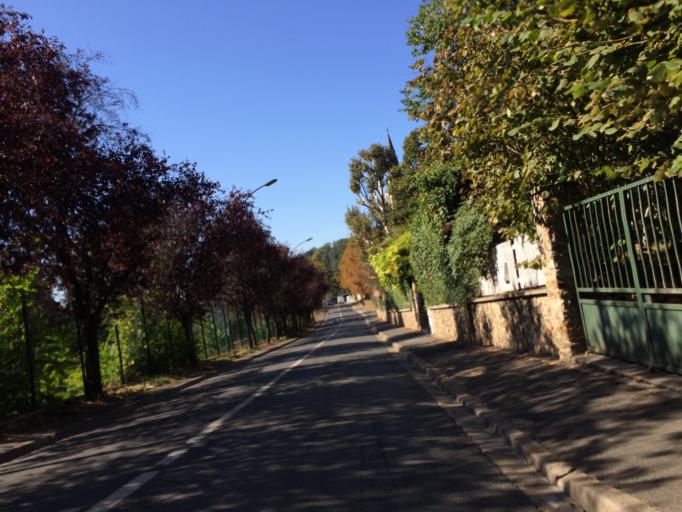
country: FR
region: Ile-de-France
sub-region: Departement de l'Essonne
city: Villebon-sur-Yvette
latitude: 48.7136
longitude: 2.2421
